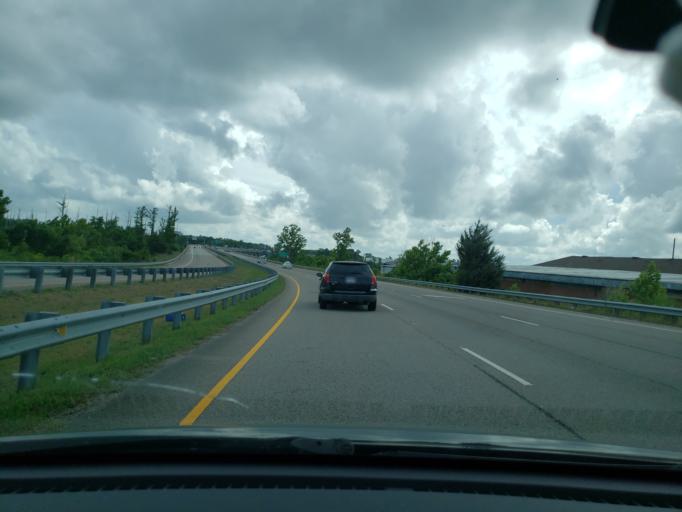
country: US
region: North Carolina
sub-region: New Hanover County
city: Wrightsboro
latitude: 34.2604
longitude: -77.9332
